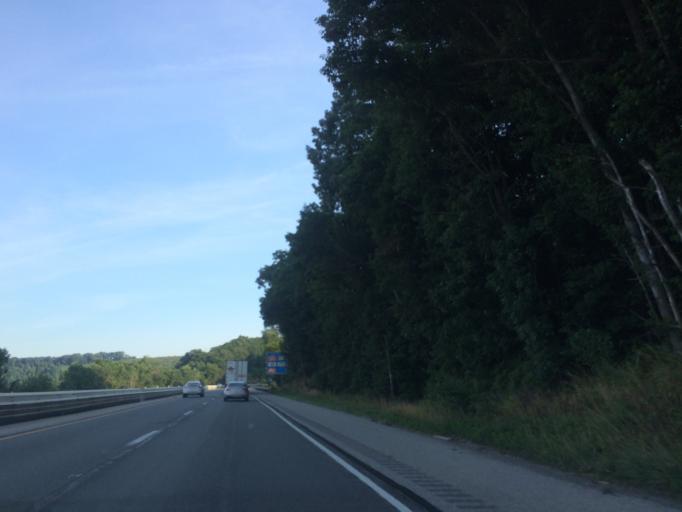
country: US
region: Pennsylvania
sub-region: York County
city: Jacobus
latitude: 39.8950
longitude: -76.7012
